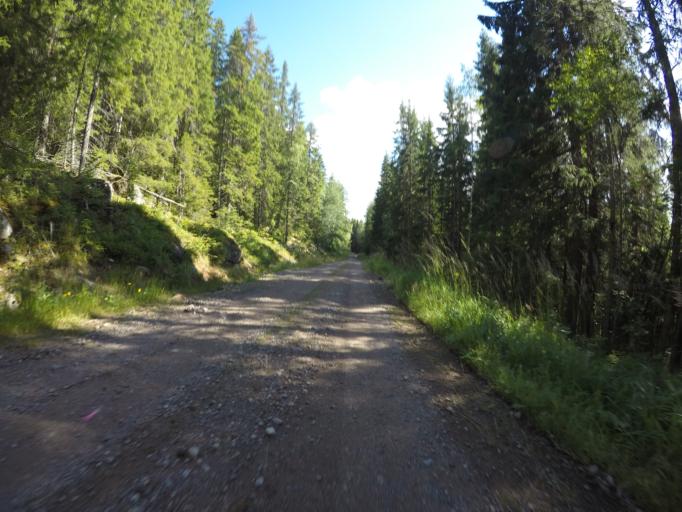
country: SE
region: OErebro
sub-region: Hallefors Kommun
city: Haellefors
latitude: 59.9892
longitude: 14.6078
